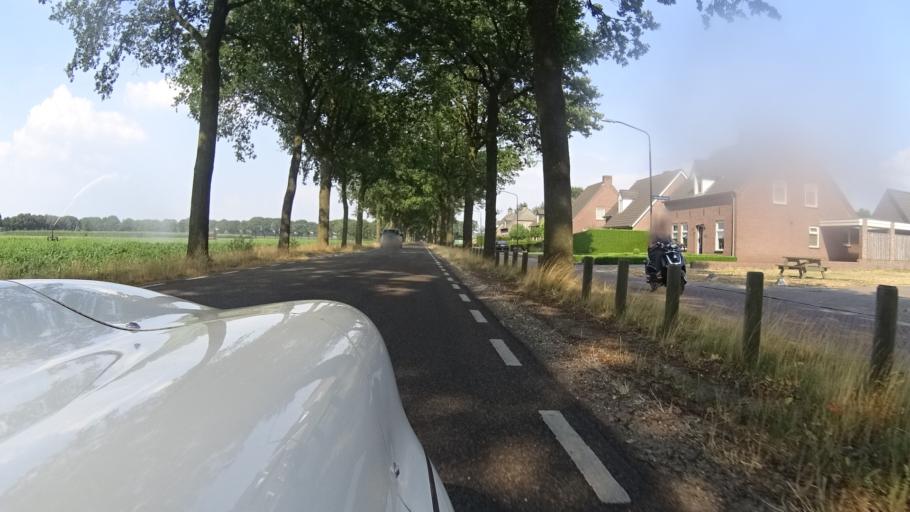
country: NL
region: North Brabant
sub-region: Gemeente Mill en Sint Hubert
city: Wilbertoord
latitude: 51.6203
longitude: 5.7921
